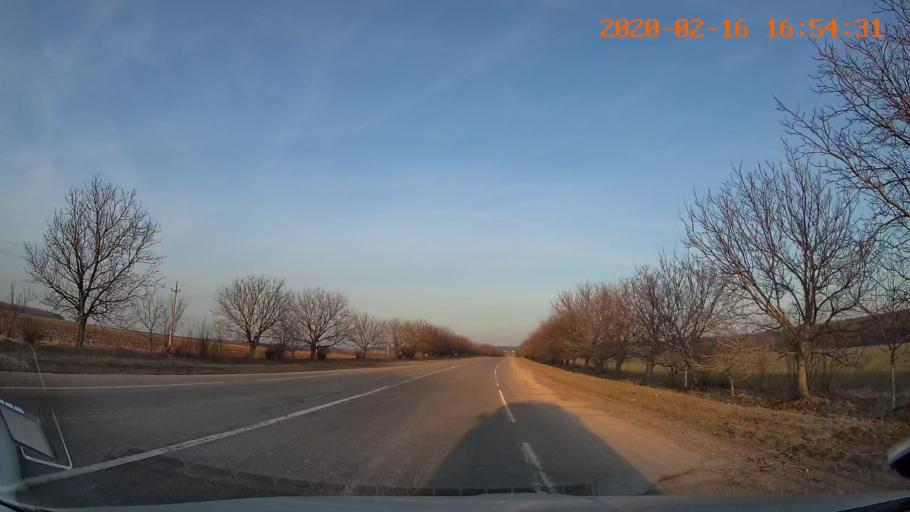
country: MD
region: Briceni
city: Briceni
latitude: 48.3218
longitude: 27.0084
